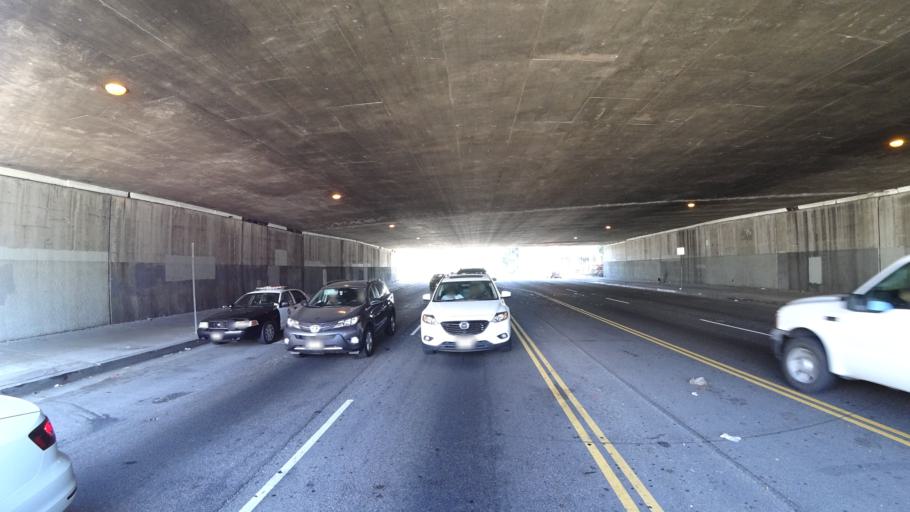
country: US
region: California
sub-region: Los Angeles County
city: Universal City
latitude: 34.1534
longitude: -118.3677
